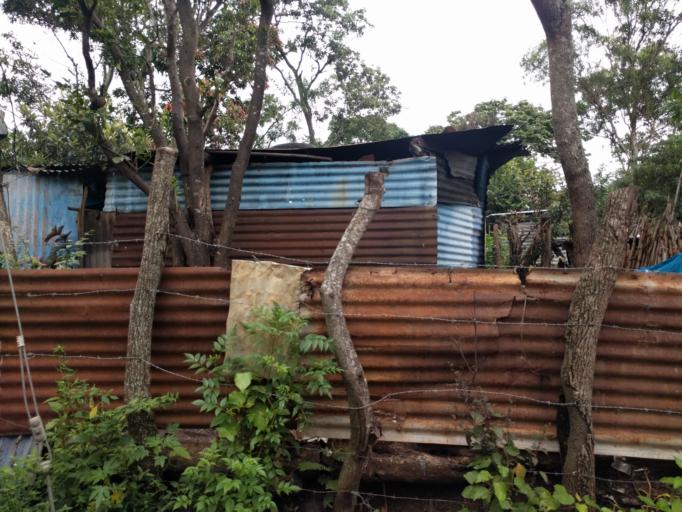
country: GT
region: Escuintla
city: San Vicente Pacaya
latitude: 14.3225
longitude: -90.5597
